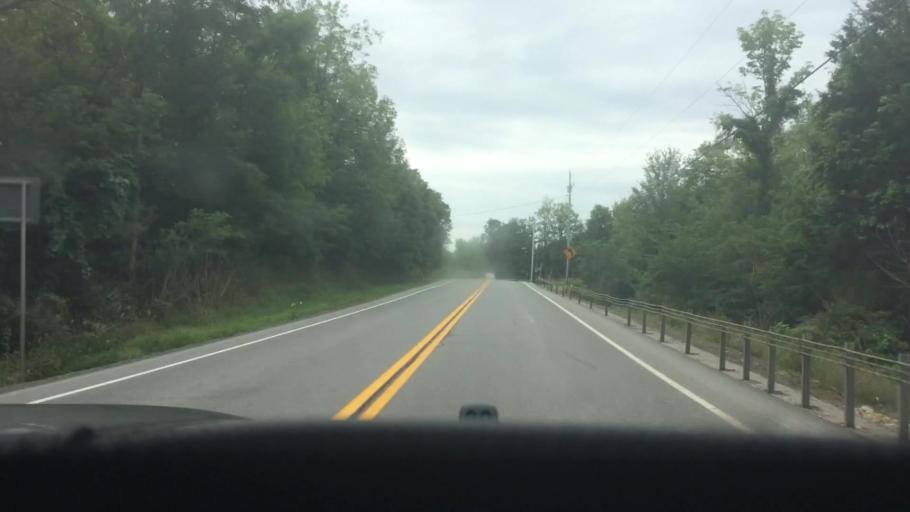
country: US
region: New York
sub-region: St. Lawrence County
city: Canton
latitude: 44.5151
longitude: -75.3393
